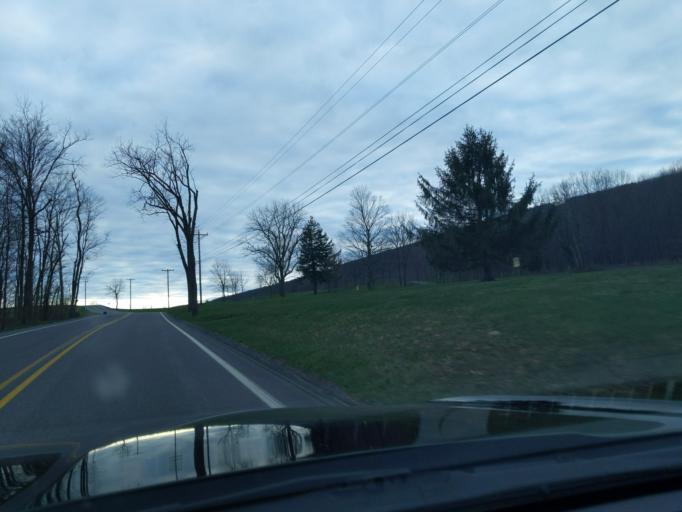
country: US
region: Pennsylvania
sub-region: Blair County
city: Lakemont
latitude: 40.4720
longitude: -78.3315
